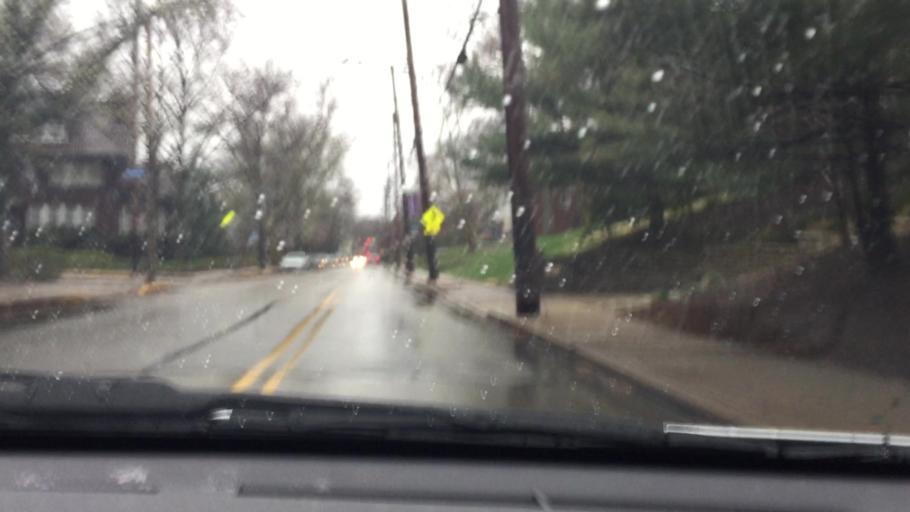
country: US
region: Pennsylvania
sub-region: Allegheny County
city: Bloomfield
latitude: 40.4440
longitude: -79.9234
